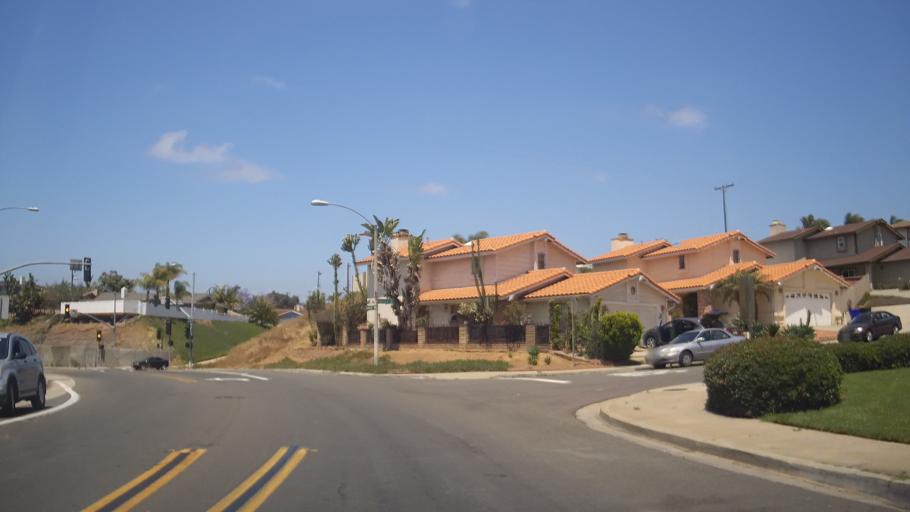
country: US
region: California
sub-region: San Diego County
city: Bonita
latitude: 32.6655
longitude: -117.0569
